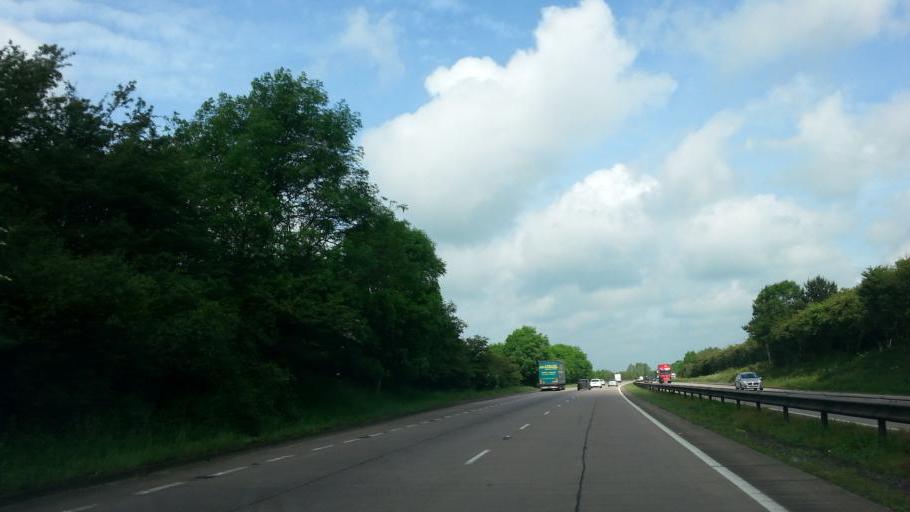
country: GB
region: England
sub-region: Staffordshire
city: Cheadle
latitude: 52.9429
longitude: -2.0021
